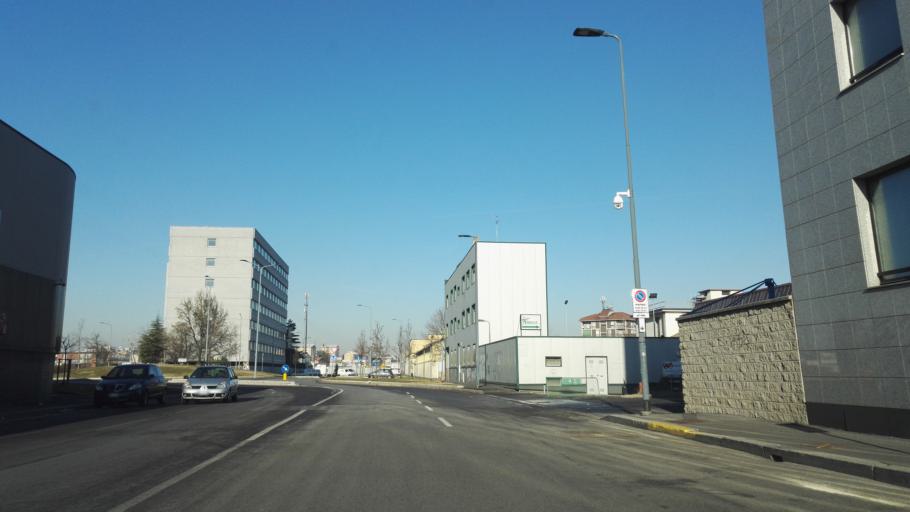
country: IT
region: Lombardy
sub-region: Citta metropolitana di Milano
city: Chiaravalle
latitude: 45.4431
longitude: 9.2325
